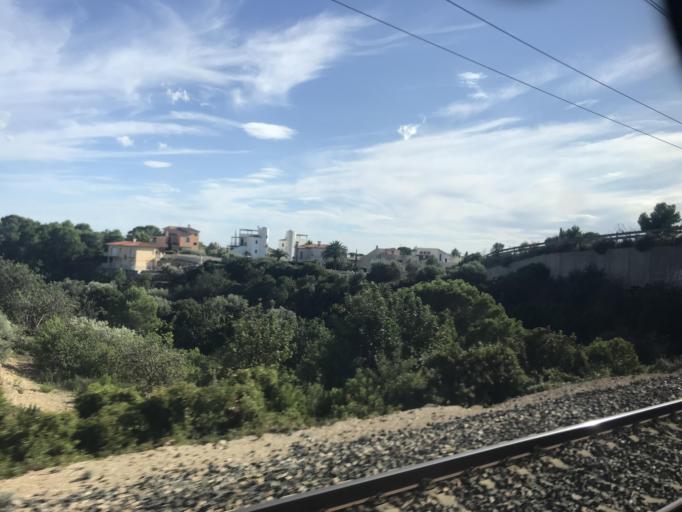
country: ES
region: Catalonia
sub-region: Provincia de Tarragona
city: L'Ampolla
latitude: 40.8181
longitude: 0.7185
